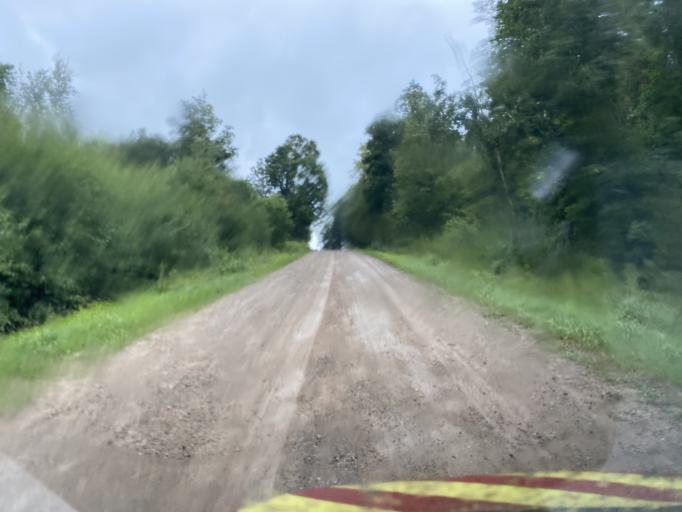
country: EE
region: Valgamaa
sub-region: Torva linn
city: Torva
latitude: 58.1174
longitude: 25.8359
